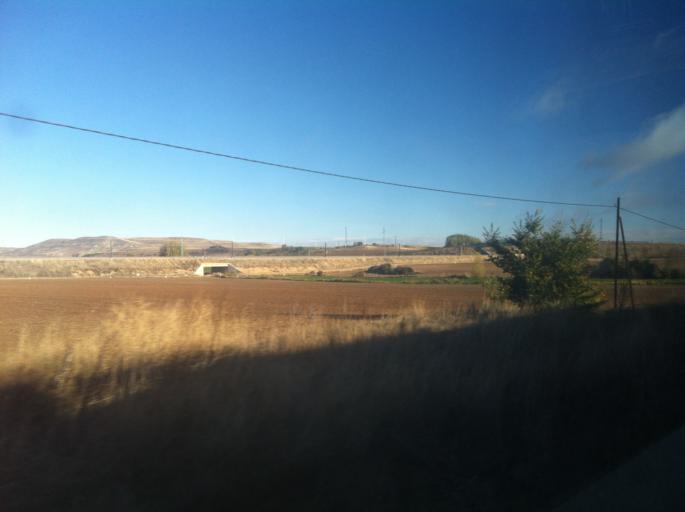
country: ES
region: Castille and Leon
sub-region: Provincia de Palencia
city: Villodrigo
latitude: 42.1377
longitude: -4.1227
